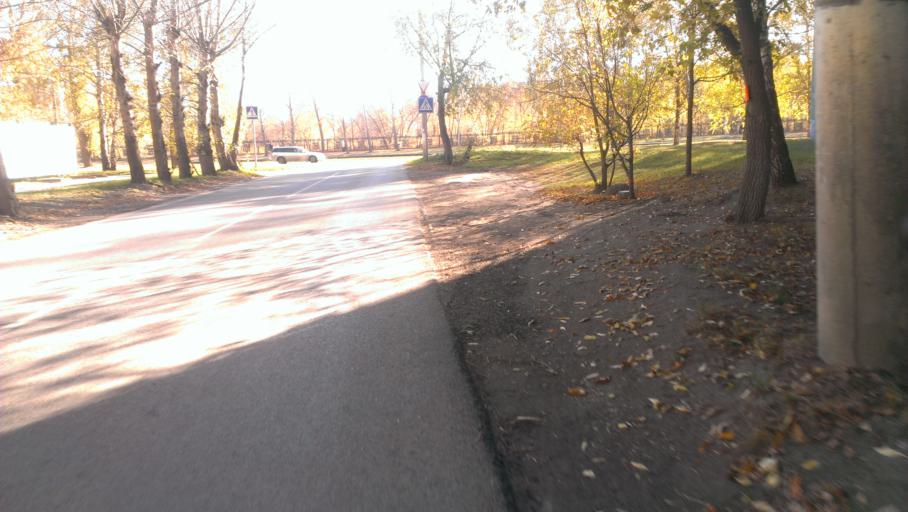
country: RU
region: Altai Krai
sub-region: Gorod Barnaulskiy
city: Barnaul
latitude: 53.3616
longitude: 83.6872
